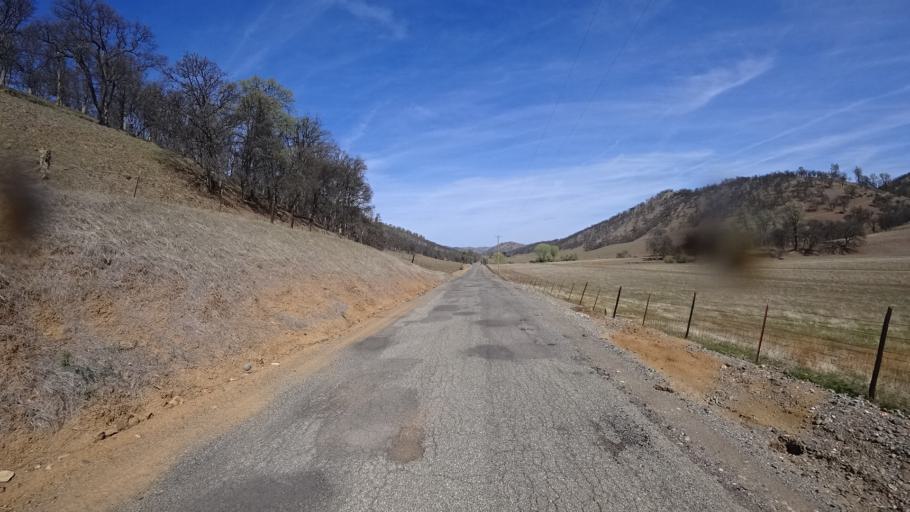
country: US
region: California
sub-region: Glenn County
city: Willows
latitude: 39.4920
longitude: -122.4539
